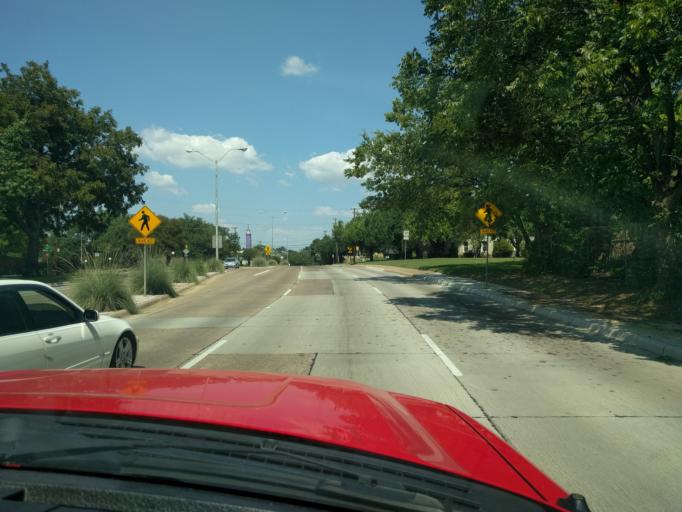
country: US
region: Texas
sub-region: Dallas County
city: Highland Park
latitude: 32.8091
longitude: -96.7528
